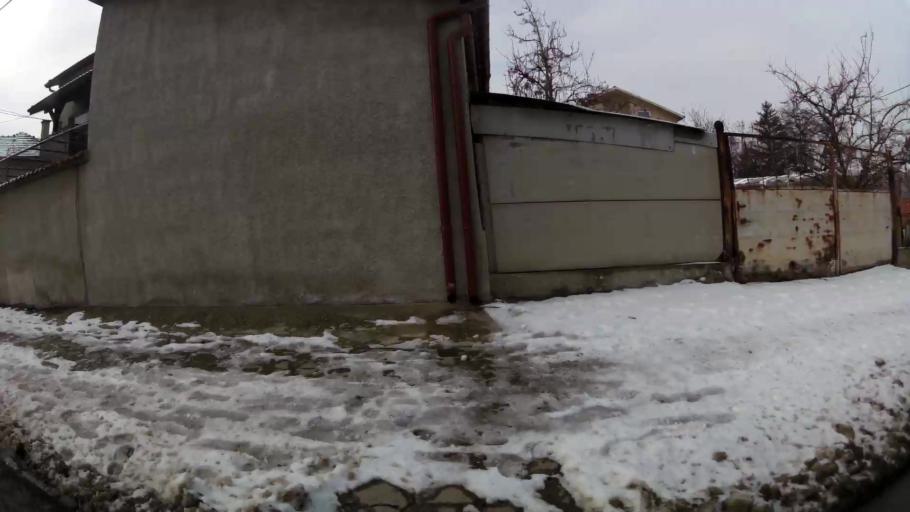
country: BG
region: Sofia-Capital
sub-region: Stolichna Obshtina
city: Sofia
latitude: 42.7128
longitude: 23.4020
